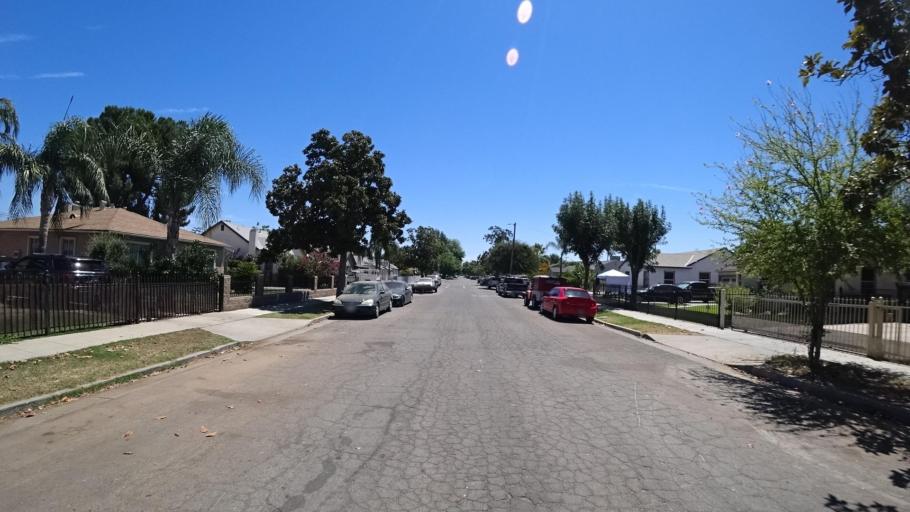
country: US
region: California
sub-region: Fresno County
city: Sunnyside
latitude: 36.7450
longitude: -119.7354
